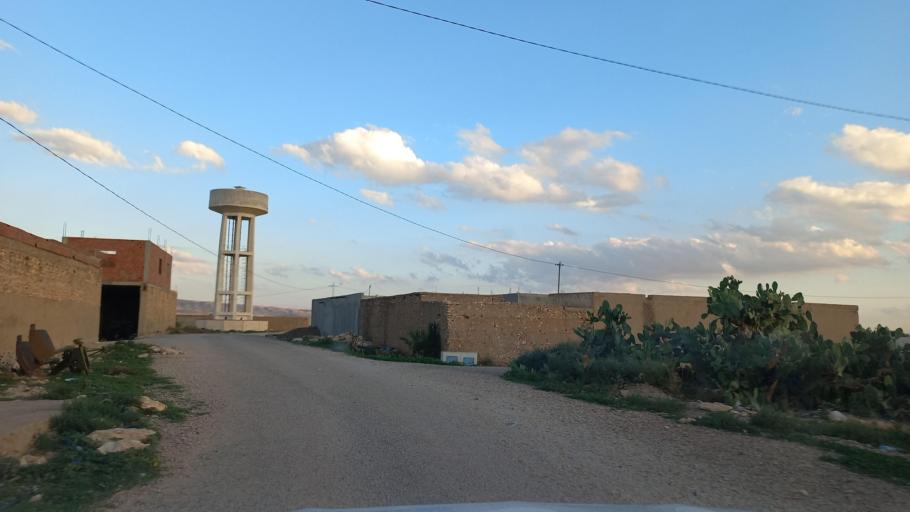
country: TN
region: Al Qasrayn
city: Sbiba
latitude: 35.3728
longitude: 9.0620
